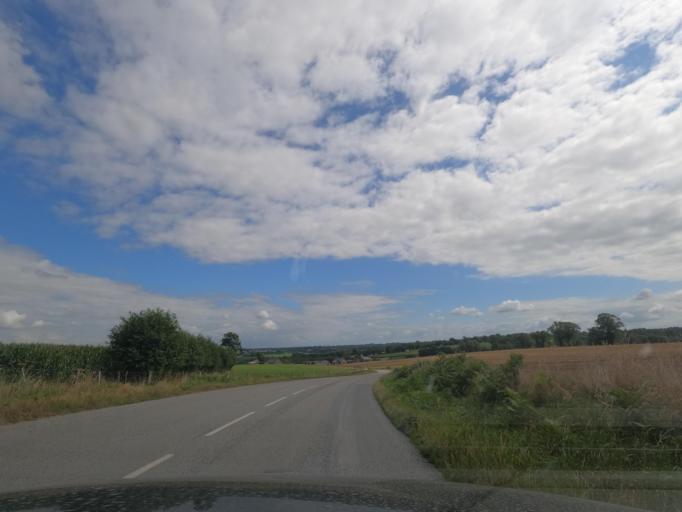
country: FR
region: Pays de la Loire
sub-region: Departement de la Mayenne
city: Landivy
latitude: 48.4782
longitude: -1.0120
